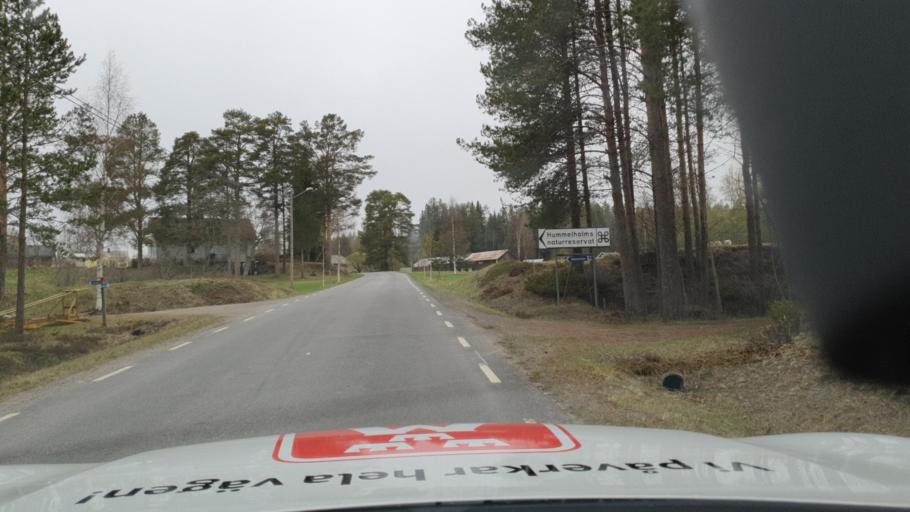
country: SE
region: Vaesterbotten
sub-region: Nordmalings Kommun
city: Nordmaling
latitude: 63.7283
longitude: 19.5089
